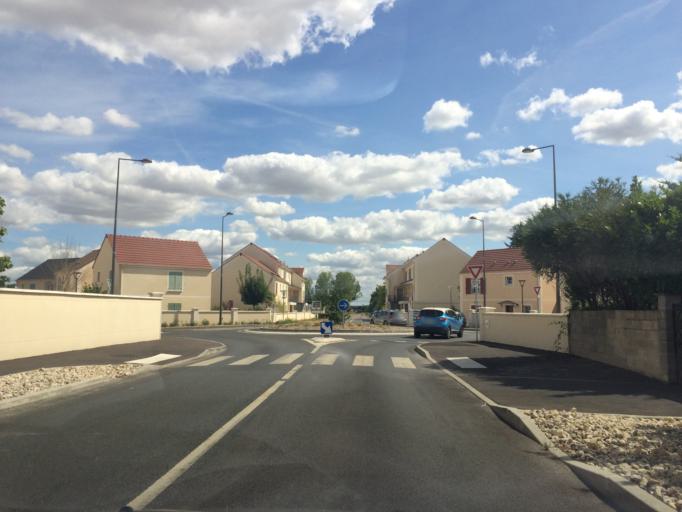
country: FR
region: Ile-de-France
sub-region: Departement de l'Essonne
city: Marolles-en-Hurepoix
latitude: 48.5571
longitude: 2.3090
